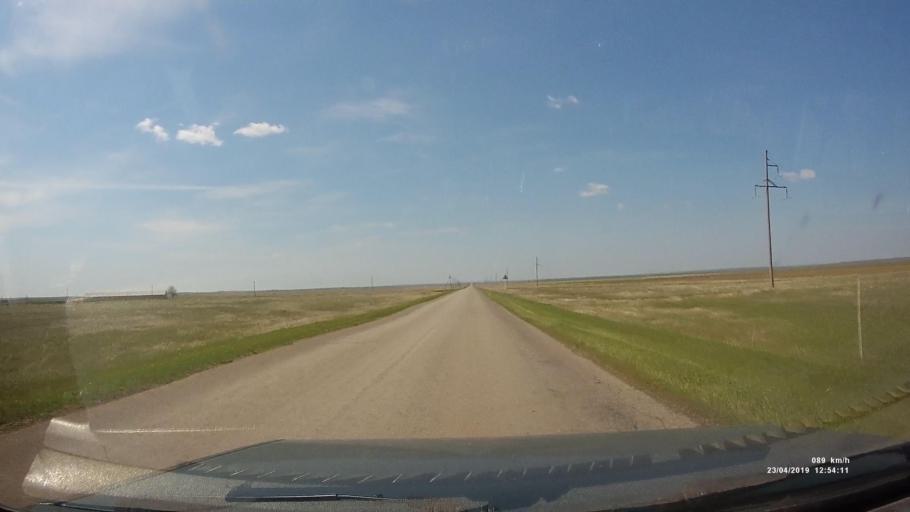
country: RU
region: Kalmykiya
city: Yashalta
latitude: 46.5786
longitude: 42.5827
